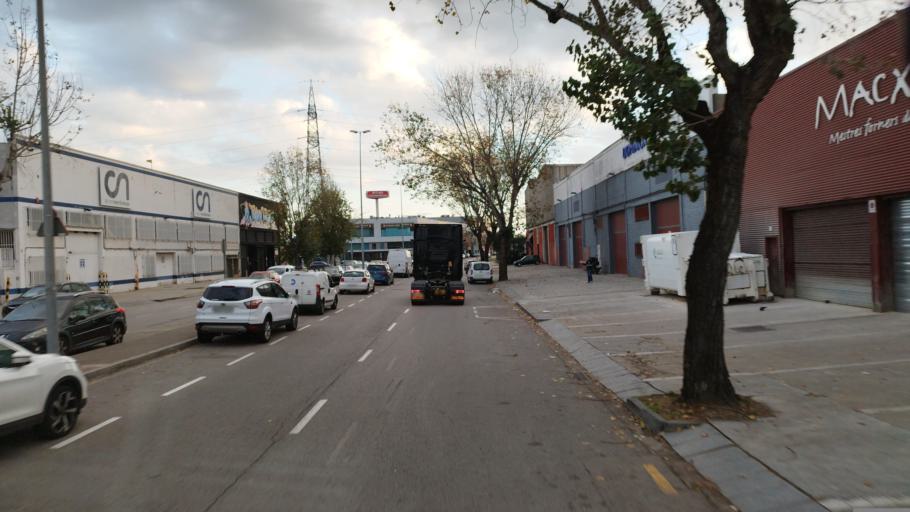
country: ES
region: Catalonia
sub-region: Provincia de Barcelona
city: Sant Boi de Llobregat
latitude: 41.3305
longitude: 2.0449
